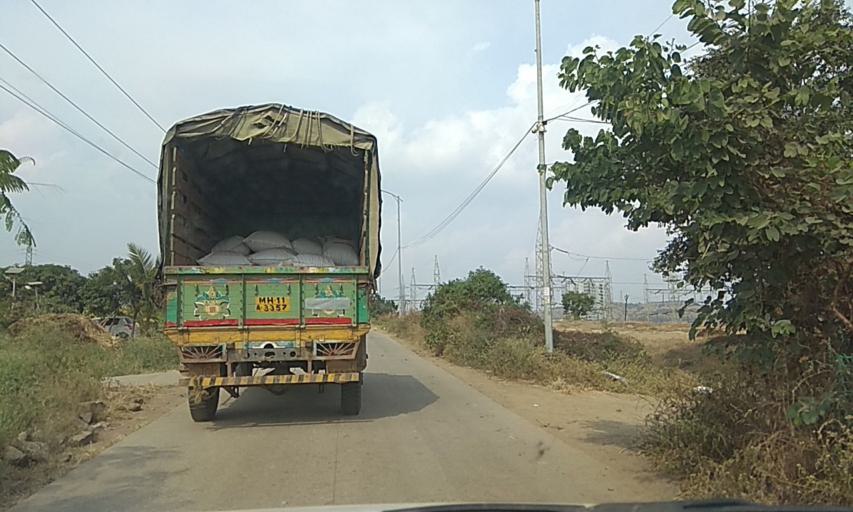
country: IN
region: Maharashtra
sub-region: Pune Division
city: Pimpri
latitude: 18.5860
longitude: 73.7059
